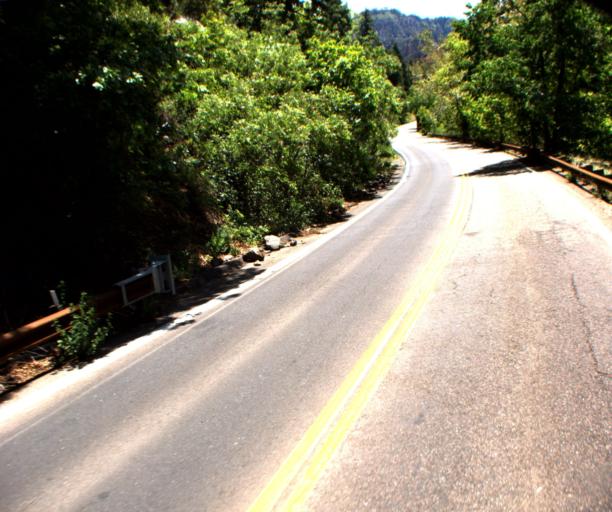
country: US
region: Arizona
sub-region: Coconino County
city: Sedona
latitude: 34.9600
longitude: -111.7532
